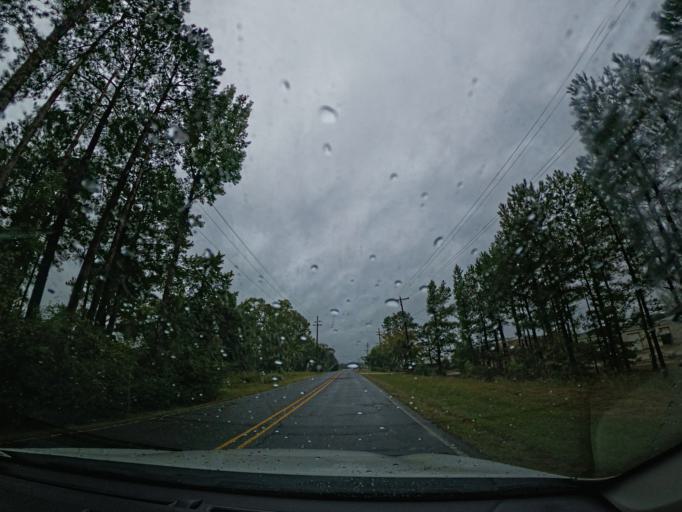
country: US
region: Louisiana
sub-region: Webster Parish
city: Minden
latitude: 32.6295
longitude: -93.2498
